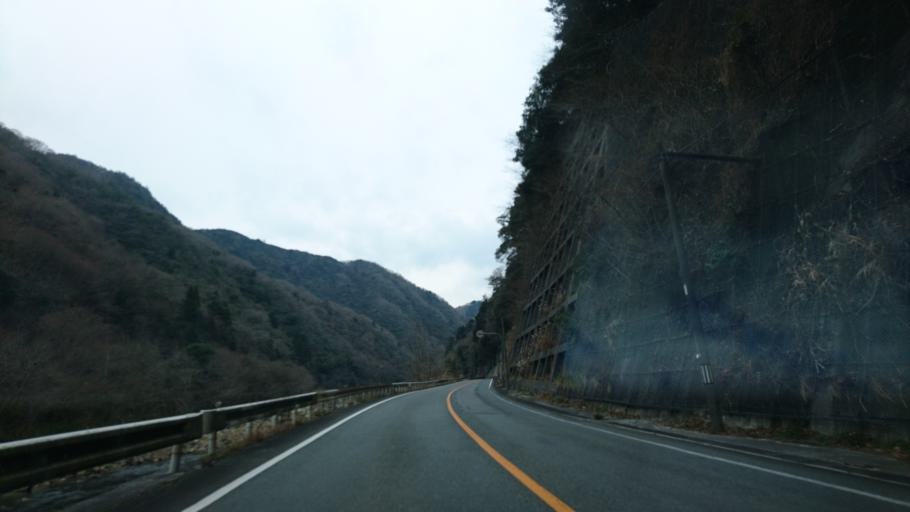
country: JP
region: Okayama
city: Niimi
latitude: 34.8964
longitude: 133.5431
